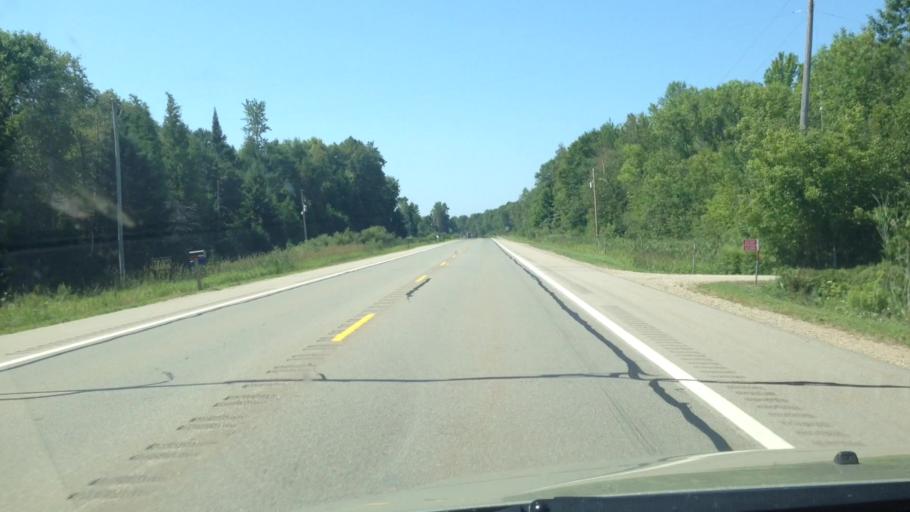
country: US
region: Michigan
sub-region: Menominee County
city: Menominee
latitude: 45.2343
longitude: -87.5052
